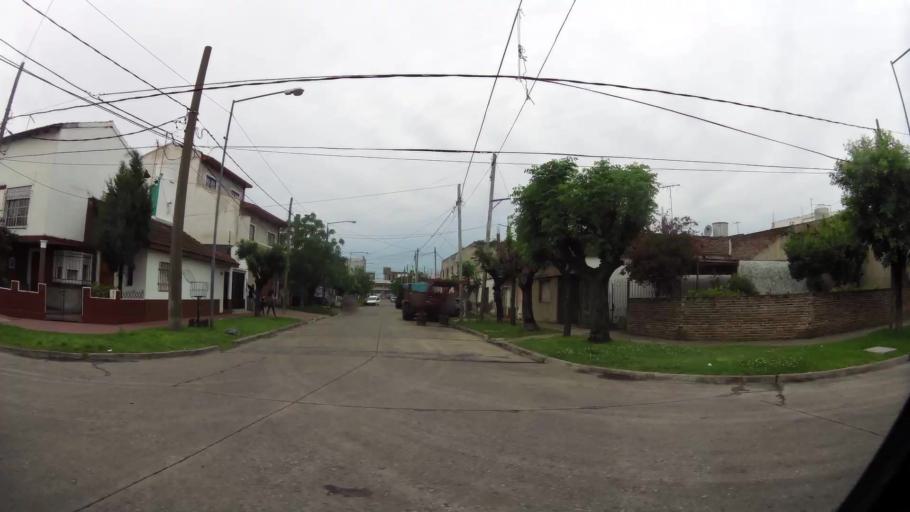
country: AR
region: Buenos Aires
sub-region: Partido de Lanus
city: Lanus
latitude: -34.7021
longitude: -58.3674
